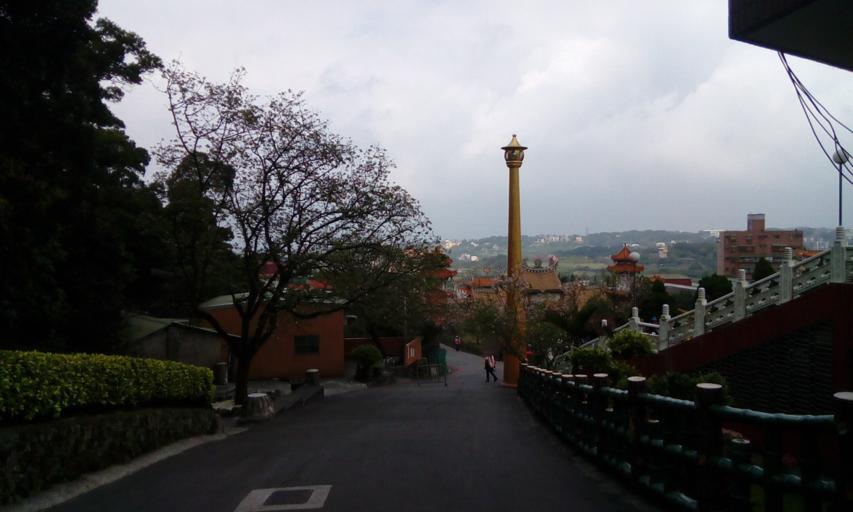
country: TW
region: Taipei
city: Taipei
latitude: 25.1855
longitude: 121.4857
